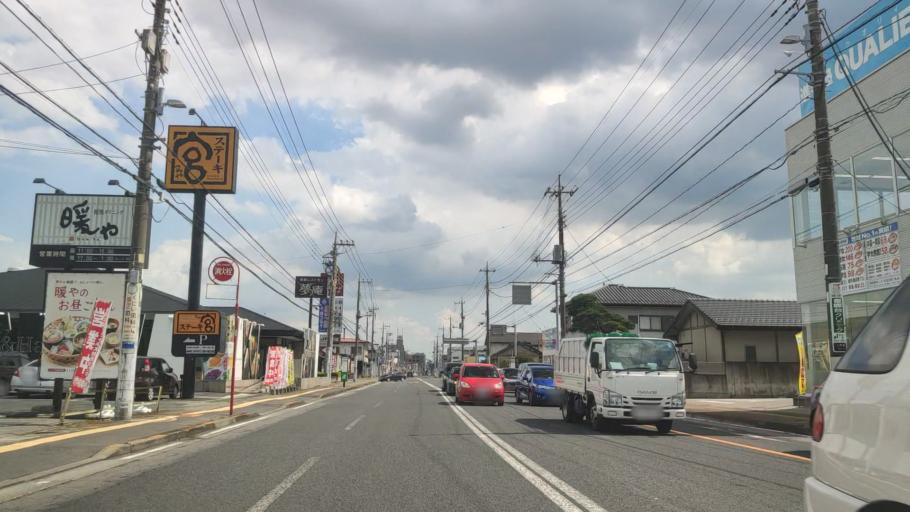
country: JP
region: Tochigi
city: Utsunomiya-shi
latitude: 36.5856
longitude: 139.8662
